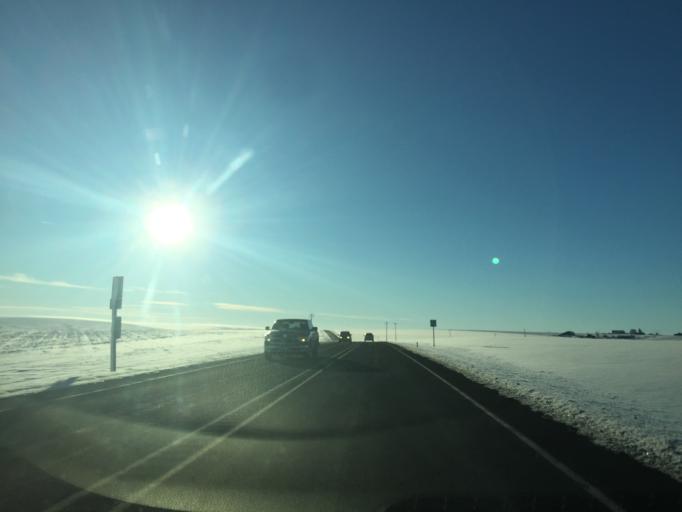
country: US
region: Washington
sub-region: Okanogan County
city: Coulee Dam
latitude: 47.7007
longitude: -118.9541
